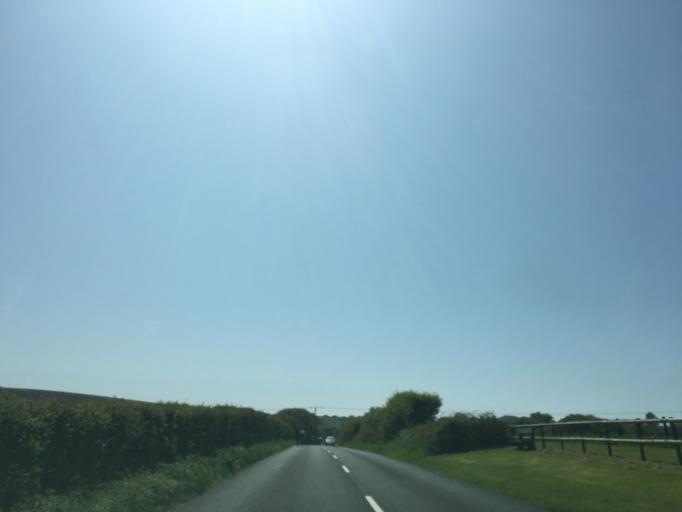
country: GB
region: England
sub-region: Isle of Wight
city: Niton
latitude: 50.5928
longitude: -1.2758
